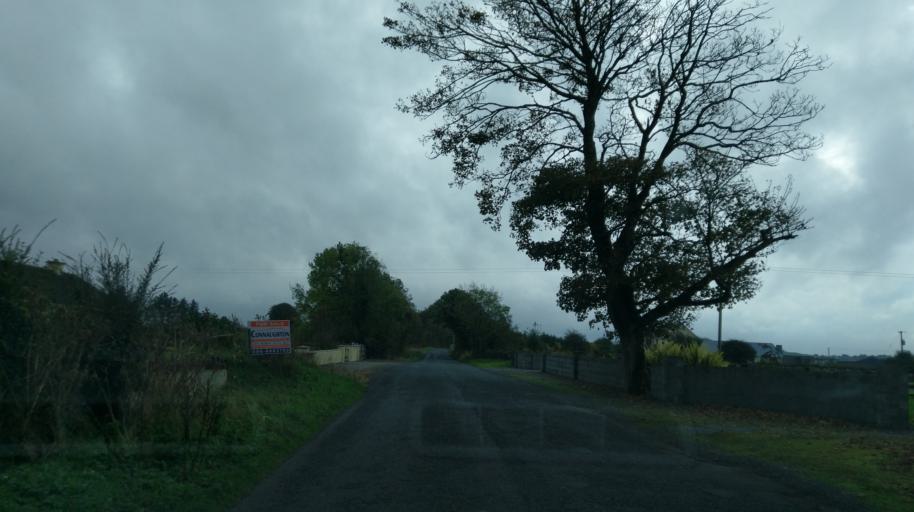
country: IE
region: Connaught
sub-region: County Galway
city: Athenry
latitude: 53.4529
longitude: -8.5820
